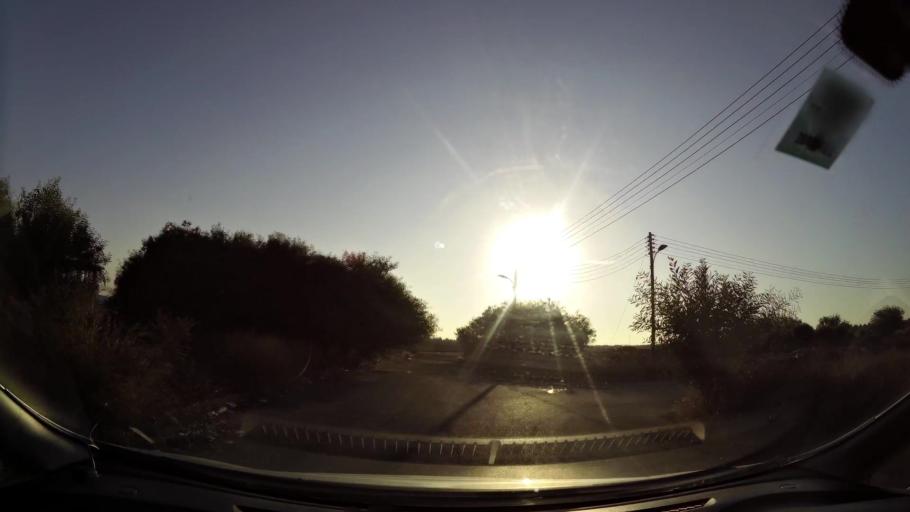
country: CY
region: Lefkosia
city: Nicosia
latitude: 35.1944
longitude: 33.3269
